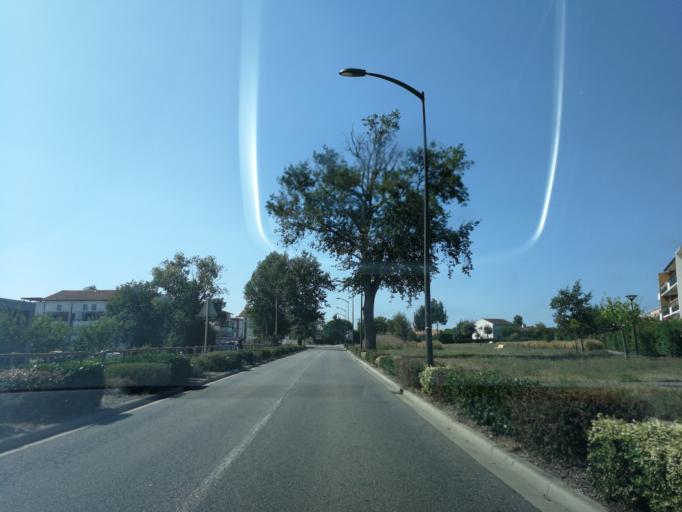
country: FR
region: Midi-Pyrenees
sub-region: Departement de la Haute-Garonne
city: Saint-Orens-de-Gameville
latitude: 43.5802
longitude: 1.5384
